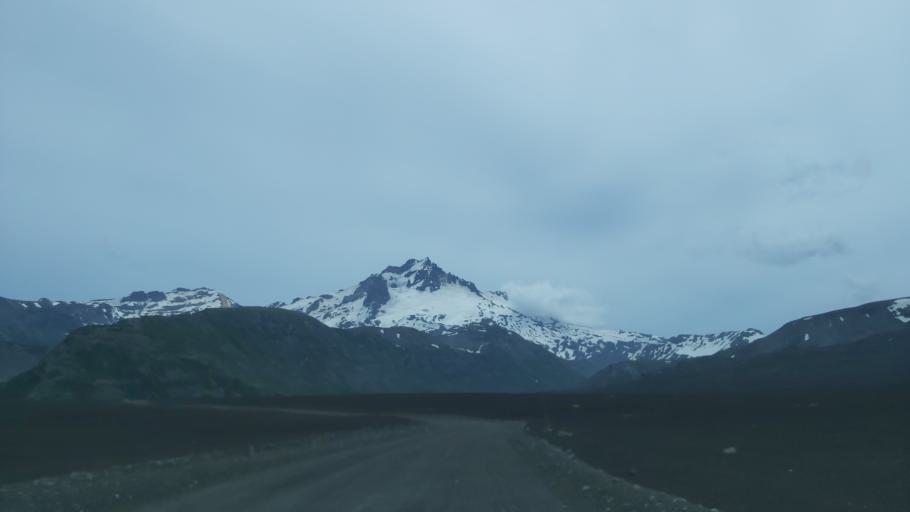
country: AR
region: Neuquen
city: Andacollo
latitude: -37.4584
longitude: -71.3016
